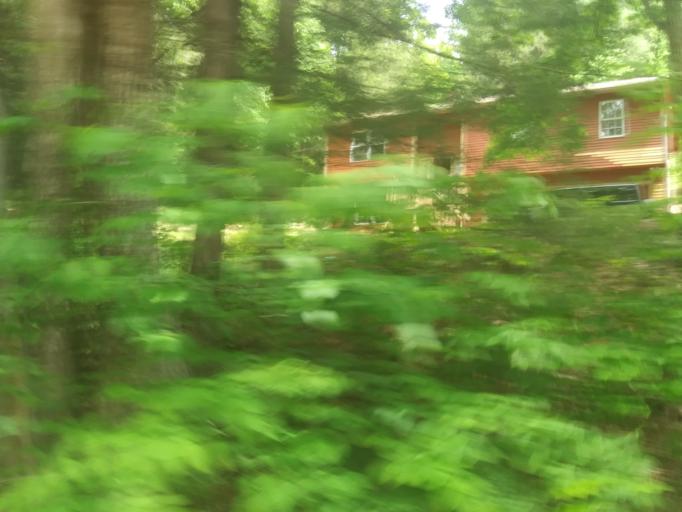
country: US
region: Massachusetts
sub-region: Franklin County
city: Buckland
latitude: 42.5755
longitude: -72.7732
